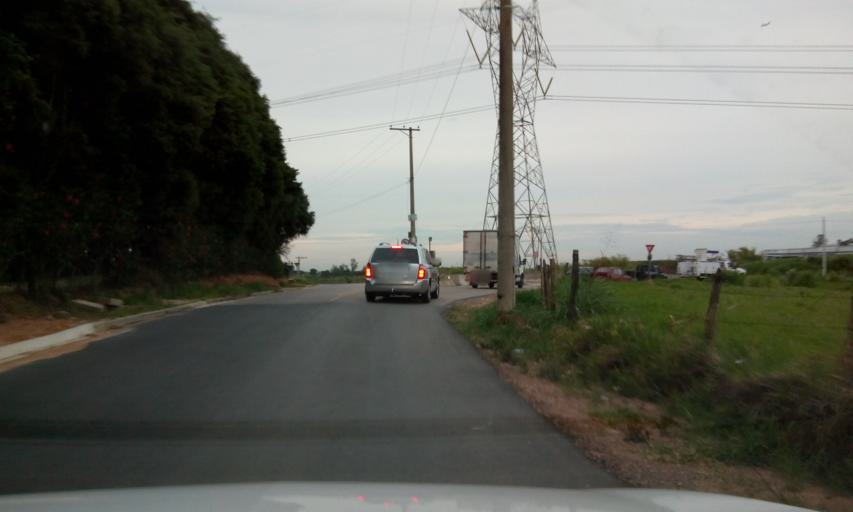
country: BR
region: Sao Paulo
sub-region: Itupeva
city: Itupeva
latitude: -23.1212
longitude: -47.0072
